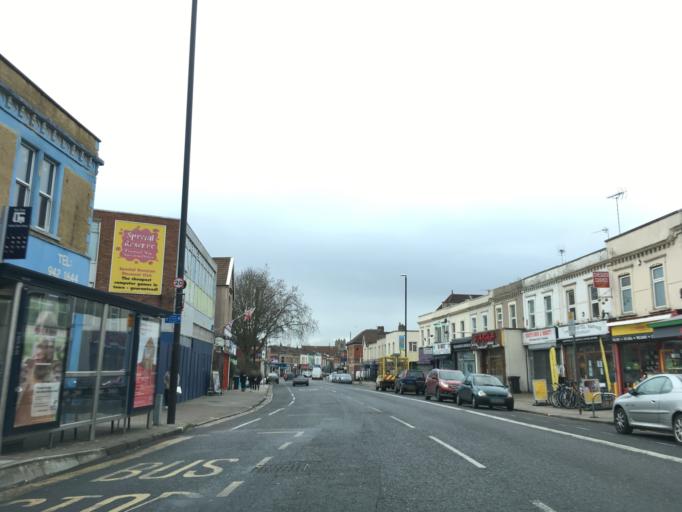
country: GB
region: England
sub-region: Bristol
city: Bristol
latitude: 51.4826
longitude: -2.5875
